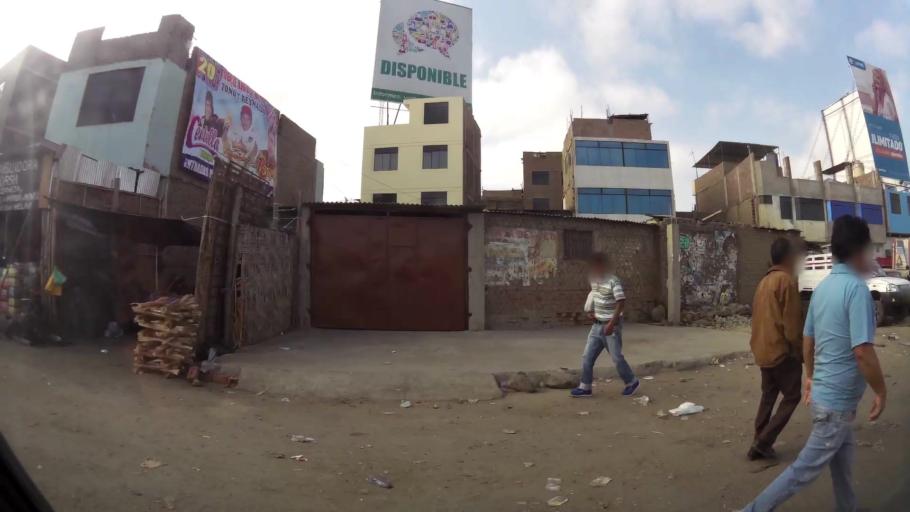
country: PE
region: La Libertad
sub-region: Provincia de Trujillo
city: Trujillo
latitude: -8.0932
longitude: -79.0253
